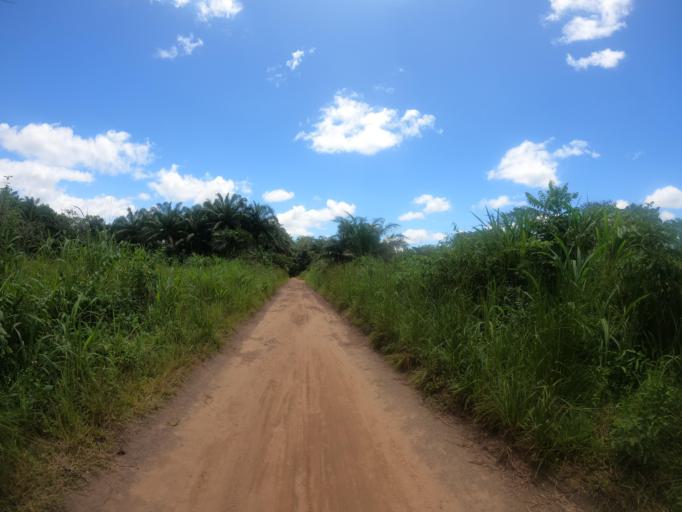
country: SL
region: Northern Province
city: Makeni
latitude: 8.8549
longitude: -12.1143
